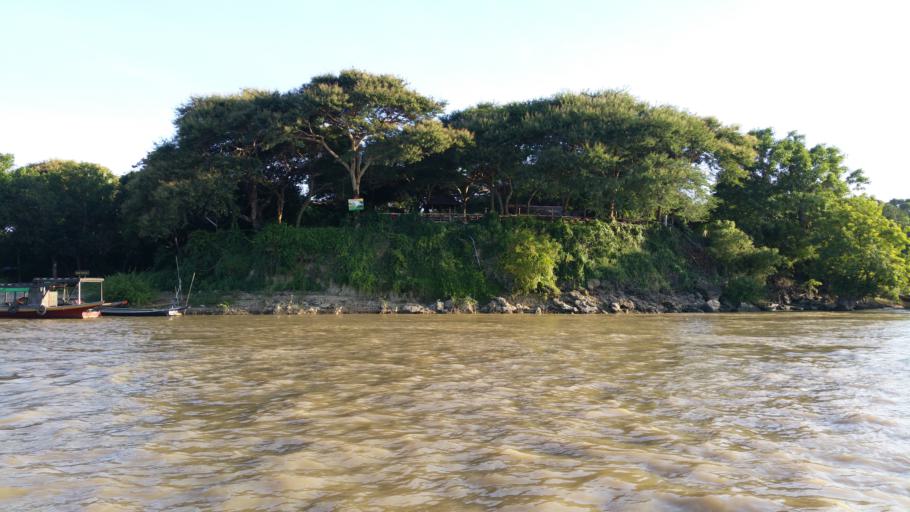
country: MM
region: Magway
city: Pakokku
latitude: 21.1843
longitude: 94.8675
